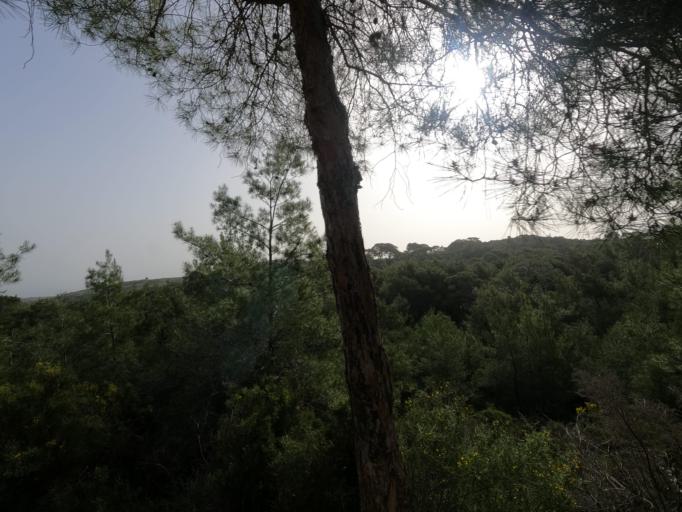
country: CY
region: Pafos
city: Polis
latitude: 34.9981
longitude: 32.3416
